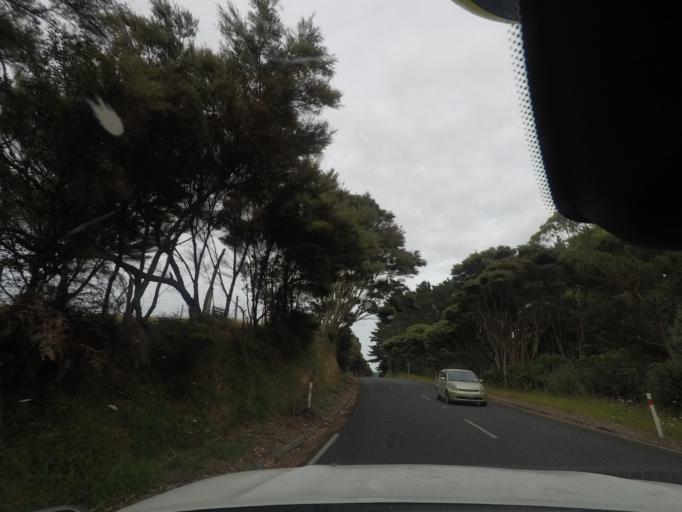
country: NZ
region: Auckland
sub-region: Auckland
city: Parakai
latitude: -36.5185
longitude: 174.2537
